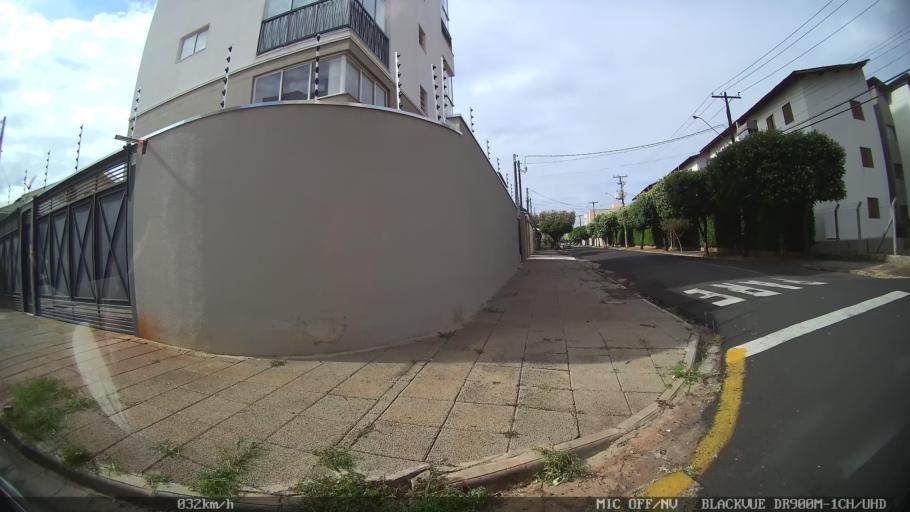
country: BR
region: Sao Paulo
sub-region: Sao Jose Do Rio Preto
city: Sao Jose do Rio Preto
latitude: -20.8307
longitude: -49.3810
